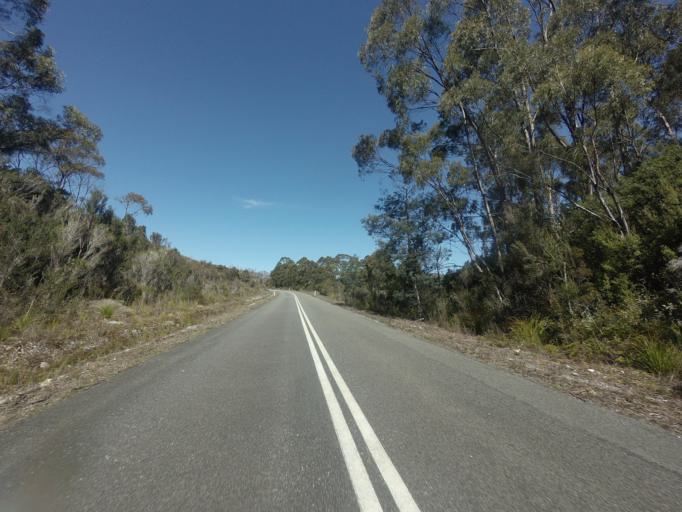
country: AU
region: Tasmania
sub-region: Huon Valley
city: Geeveston
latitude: -42.8345
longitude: 146.1539
